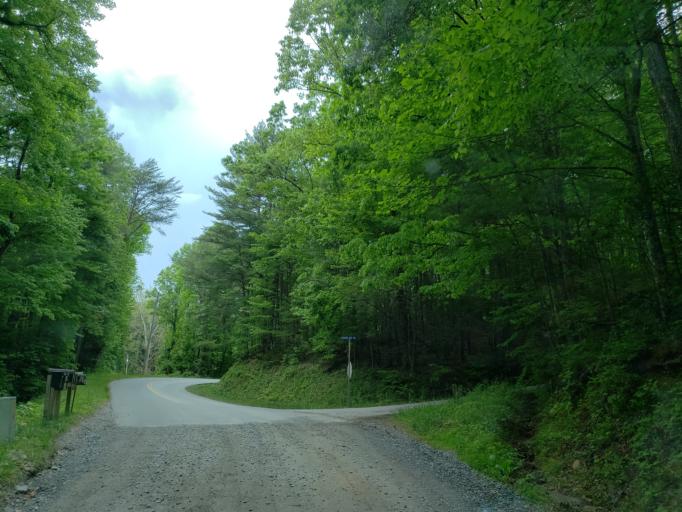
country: US
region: Georgia
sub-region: Fannin County
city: Blue Ridge
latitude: 34.8584
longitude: -84.4238
